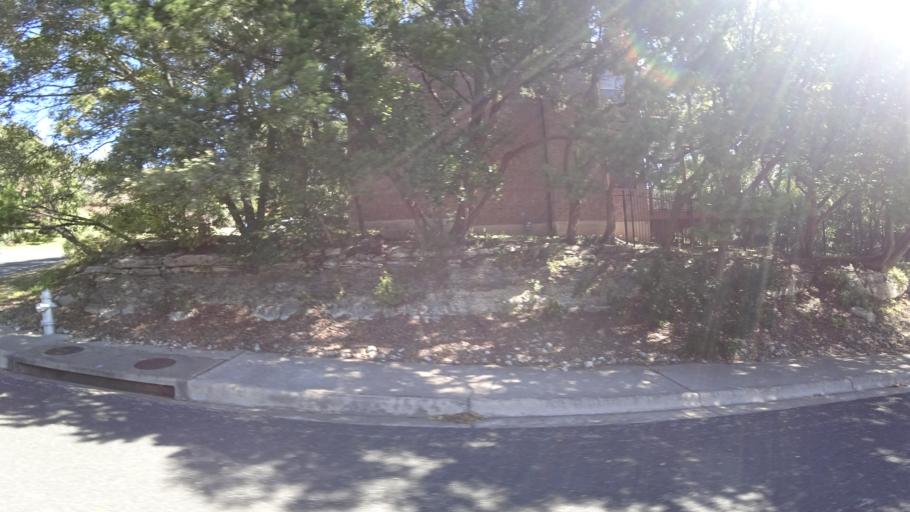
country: US
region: Texas
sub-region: Travis County
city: West Lake Hills
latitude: 30.3462
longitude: -97.7780
